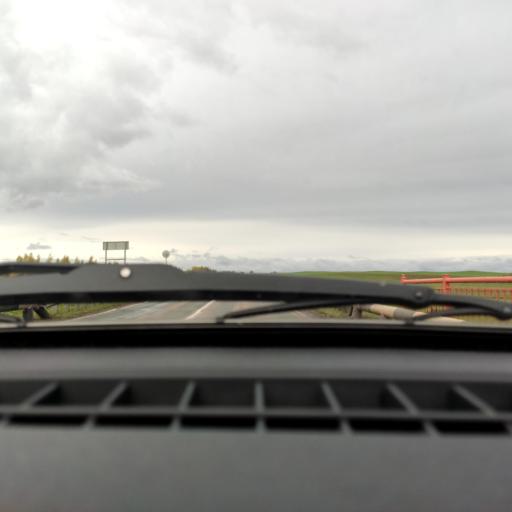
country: RU
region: Bashkortostan
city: Rayevskiy
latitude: 54.1371
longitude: 54.9413
